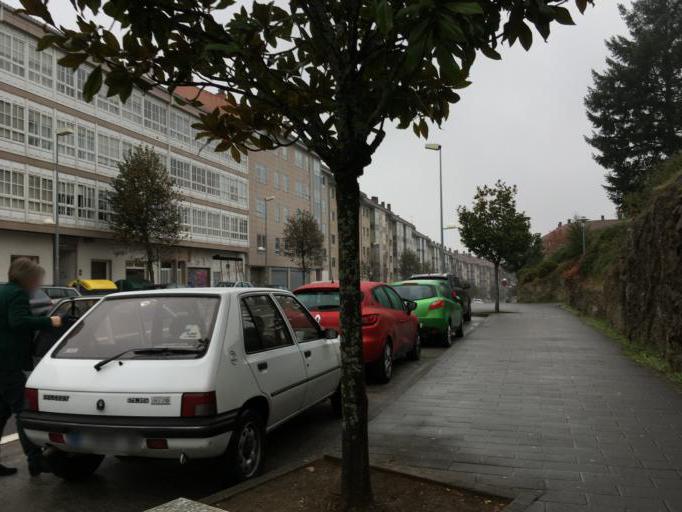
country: ES
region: Galicia
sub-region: Provincia da Coruna
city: Santiago de Compostela
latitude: 42.8701
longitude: -8.5544
